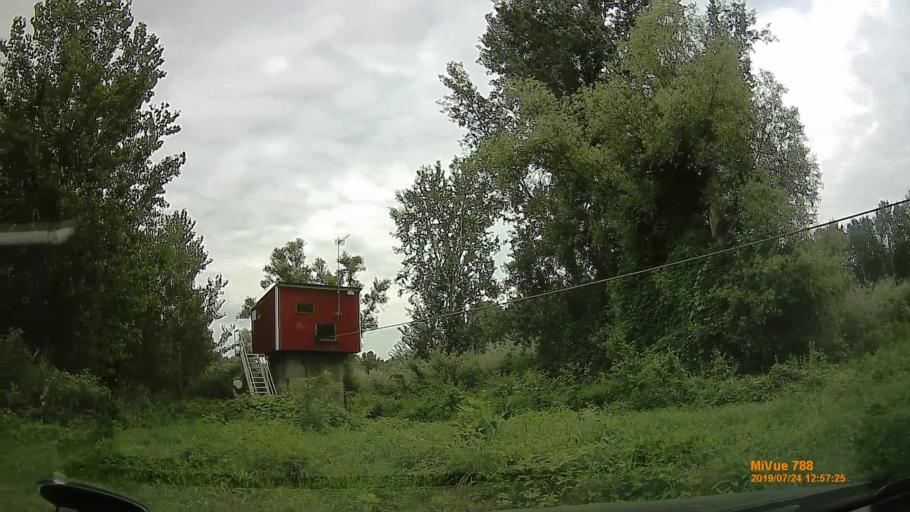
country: HU
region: Szabolcs-Szatmar-Bereg
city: Aranyosapati
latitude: 48.2203
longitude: 22.2801
